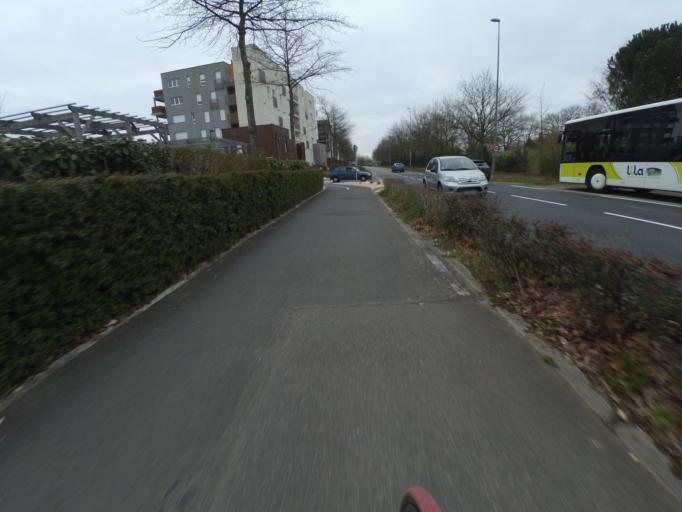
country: FR
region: Pays de la Loire
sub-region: Departement de la Loire-Atlantique
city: Carquefou
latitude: 47.2910
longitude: -1.4858
